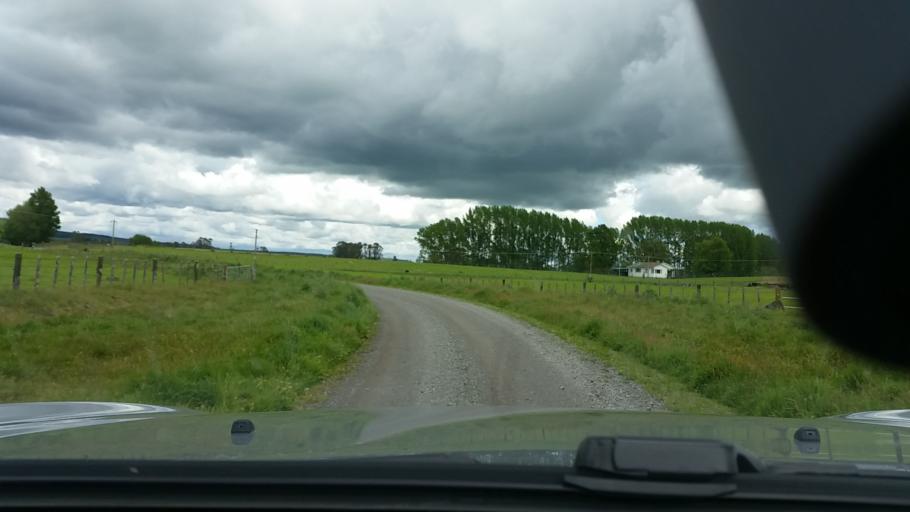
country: NZ
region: Waikato
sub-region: Taupo District
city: Taupo
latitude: -38.5221
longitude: 176.3659
